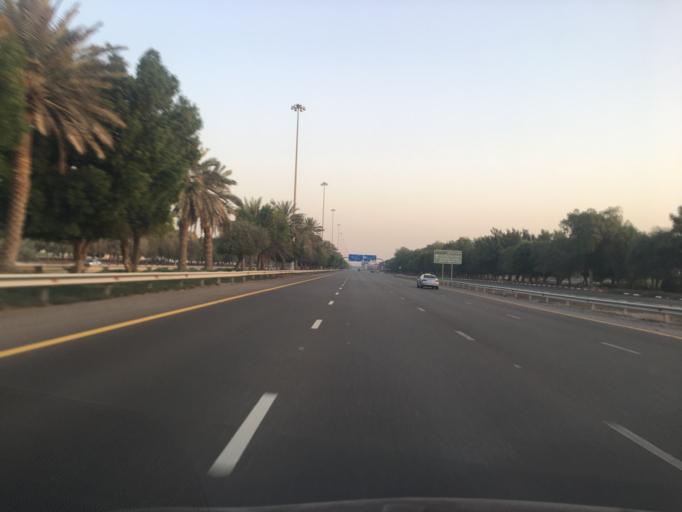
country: AE
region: Abu Dhabi
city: Abu Dhabi
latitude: 24.3784
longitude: 54.5496
